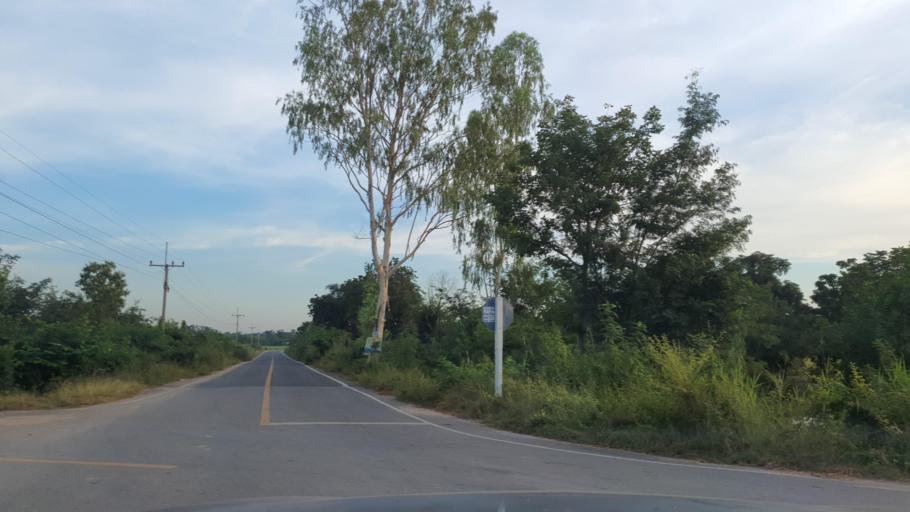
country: TH
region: Uthai Thani
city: Sawang Arom
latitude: 15.7184
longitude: 99.9532
